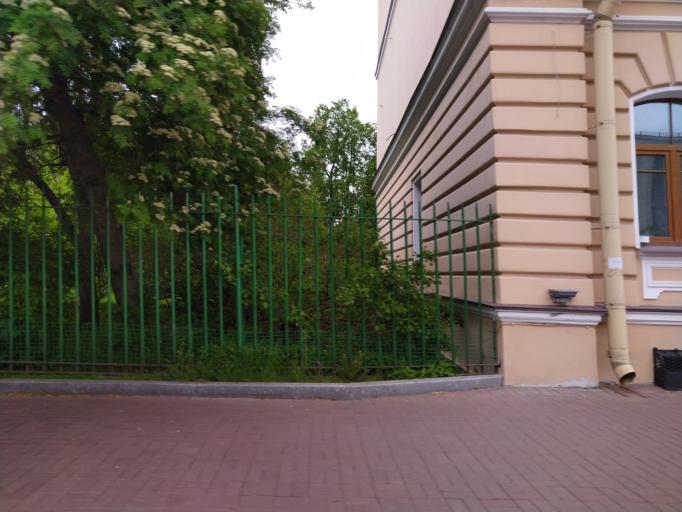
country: RU
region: Leningrad
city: Finlyandskiy
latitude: 59.9478
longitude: 30.3907
